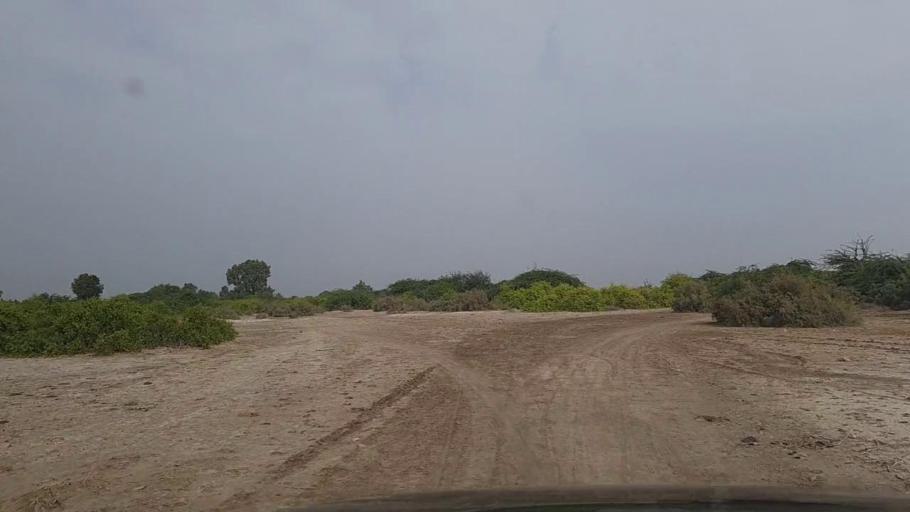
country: PK
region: Sindh
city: Thatta
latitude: 24.7538
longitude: 67.8273
